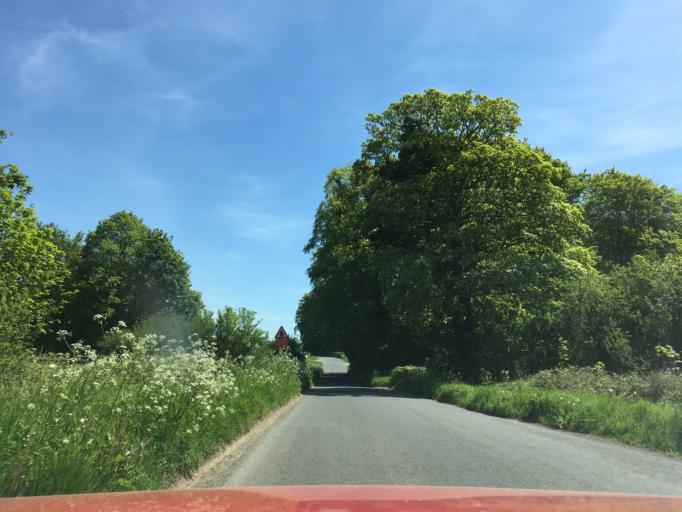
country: GB
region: England
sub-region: Gloucestershire
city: Coates
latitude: 51.7247
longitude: -2.0771
